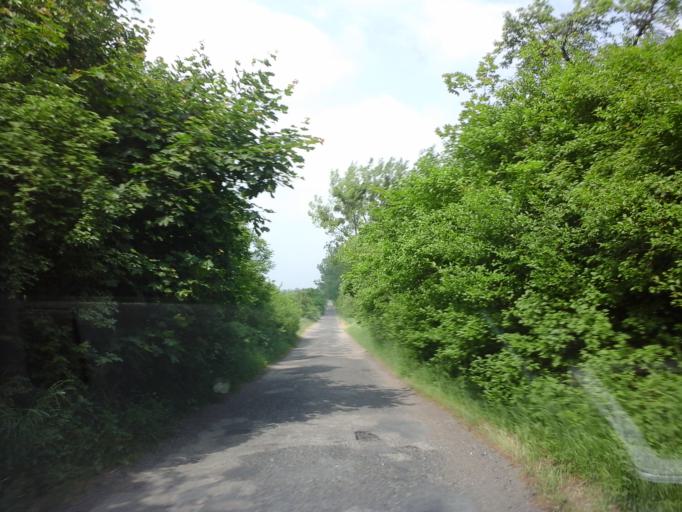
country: PL
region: West Pomeranian Voivodeship
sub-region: Powiat choszczenski
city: Pelczyce
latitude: 53.0491
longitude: 15.2485
